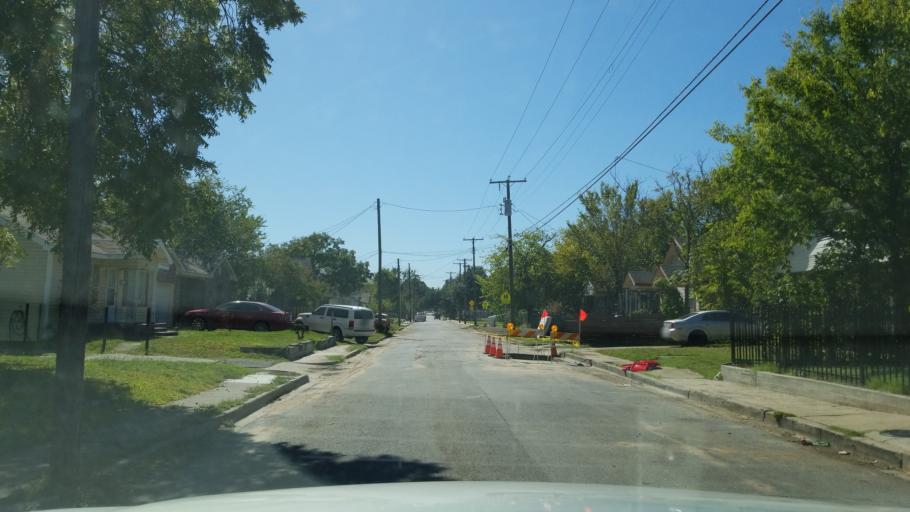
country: US
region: Texas
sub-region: Dallas County
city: Dallas
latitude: 32.7754
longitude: -96.7468
